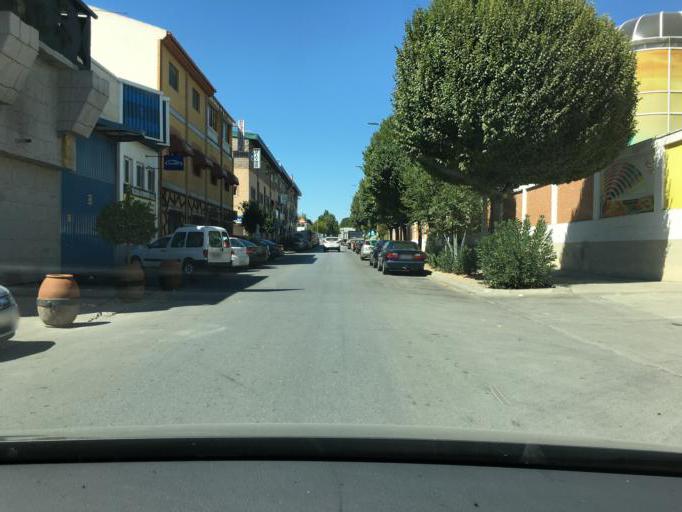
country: ES
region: Andalusia
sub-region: Provincia de Granada
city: Albolote
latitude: 37.2318
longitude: -3.6476
